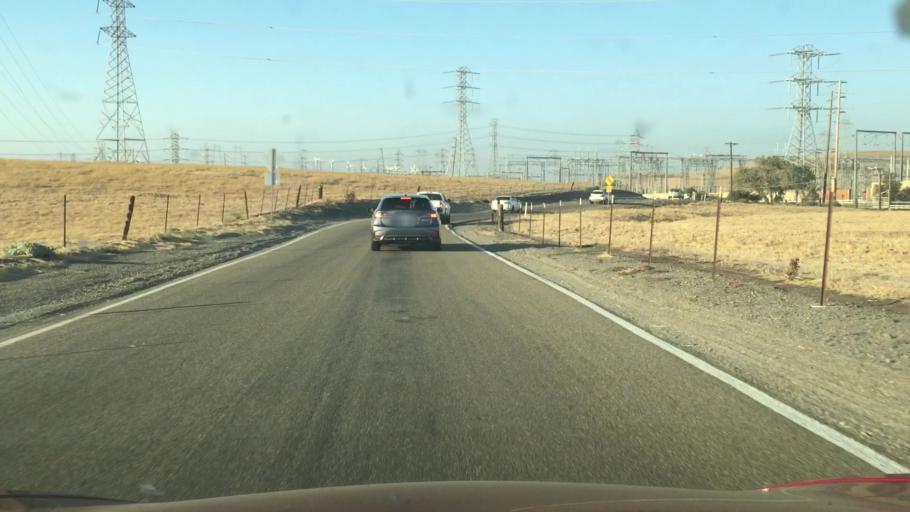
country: US
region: California
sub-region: San Joaquin County
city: Mountain House
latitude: 37.7120
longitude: -121.5695
